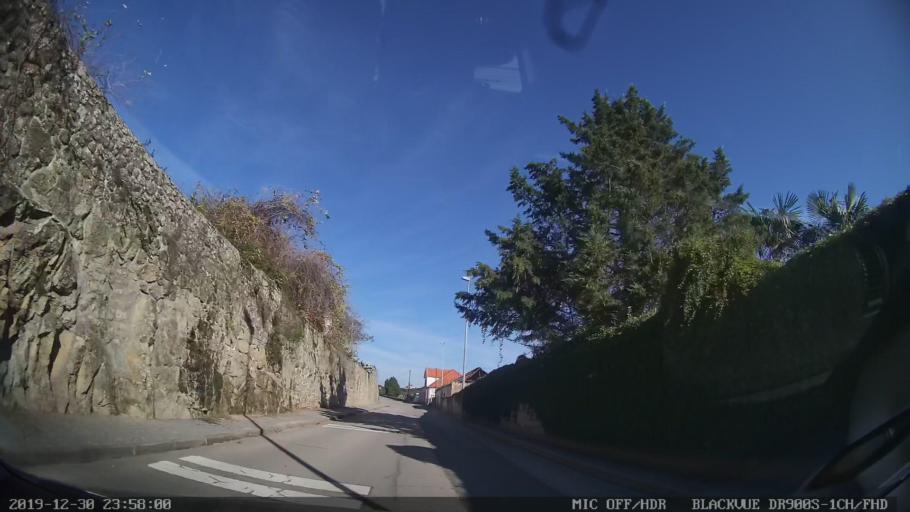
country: PT
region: Castelo Branco
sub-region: Idanha-A-Nova
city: Idanha-a-Nova
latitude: 39.9263
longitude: -7.2368
